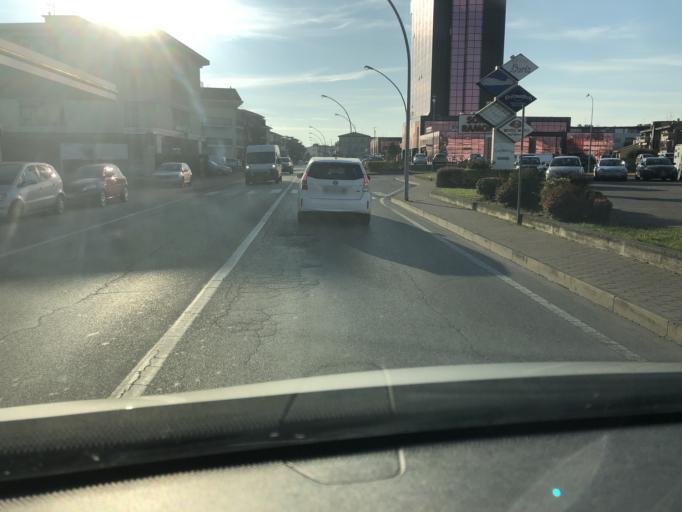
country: IT
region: Veneto
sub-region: Provincia di Verona
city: Bussolengo
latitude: 45.4688
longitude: 10.8542
